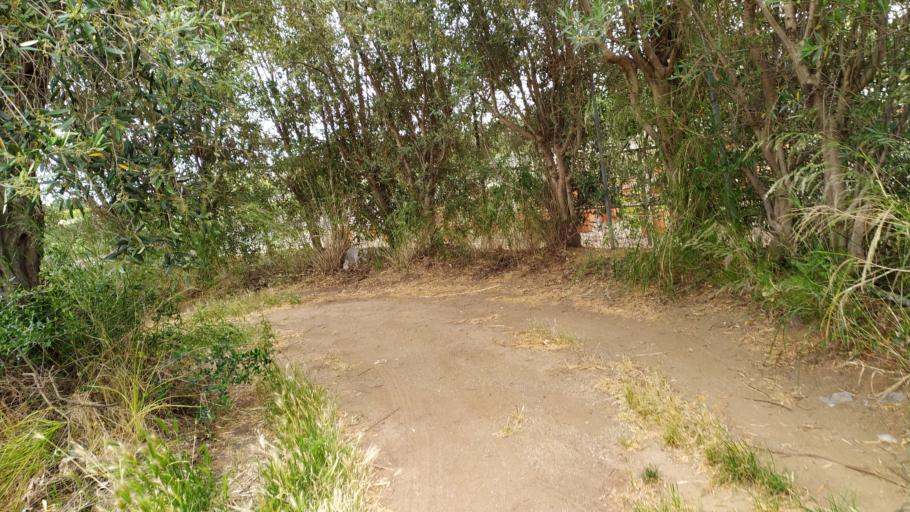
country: IT
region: Sicily
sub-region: Messina
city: San Filippo del Mela
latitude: 38.1846
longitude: 15.2639
